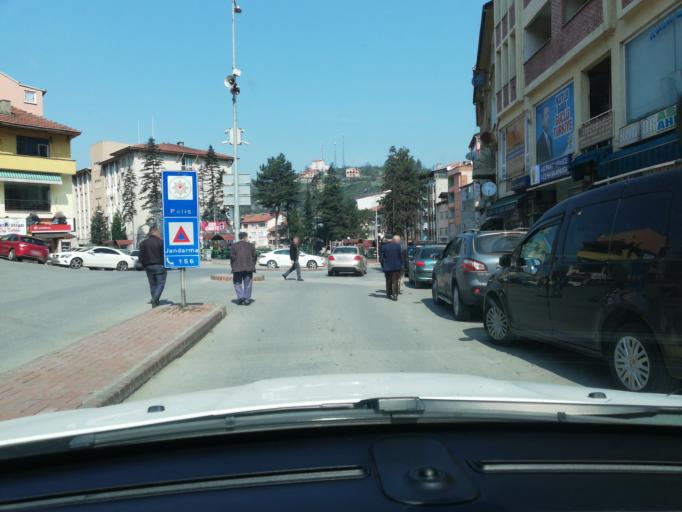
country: TR
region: Karabuk
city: Yenice
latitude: 41.1999
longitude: 32.3295
